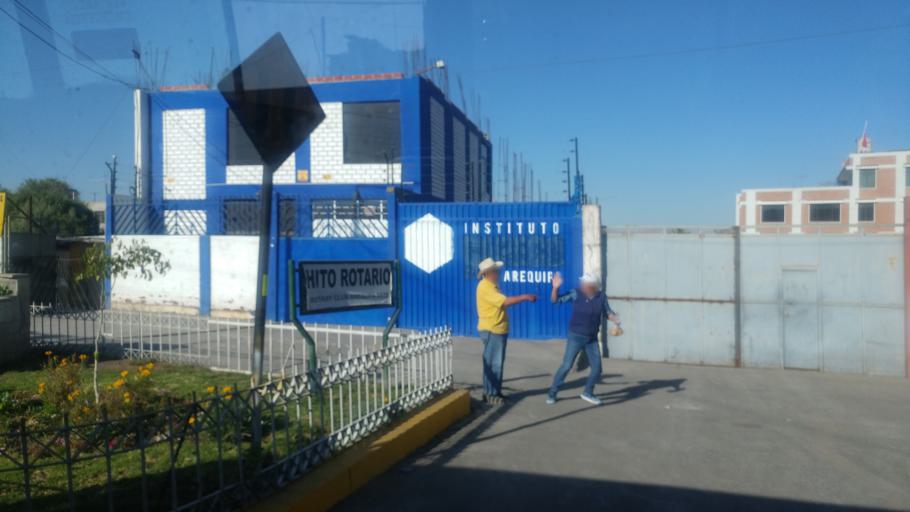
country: PE
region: Arequipa
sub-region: Provincia de Arequipa
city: Arequipa
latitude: -16.4255
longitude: -71.5051
